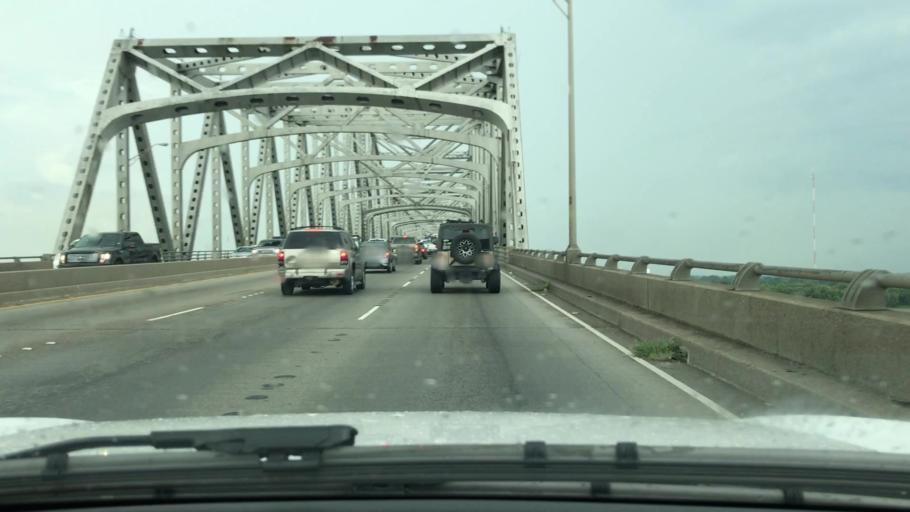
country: US
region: Louisiana
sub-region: West Baton Rouge Parish
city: Port Allen
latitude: 30.4398
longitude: -91.2030
